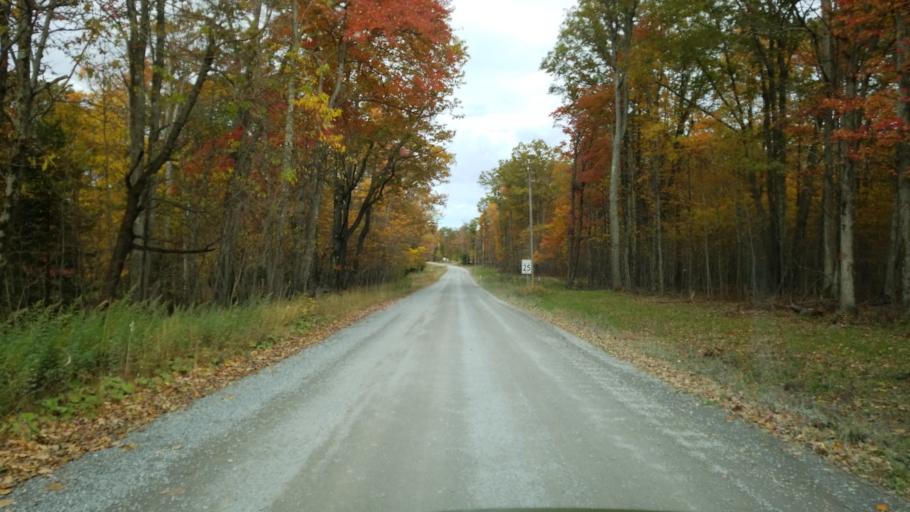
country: US
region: Pennsylvania
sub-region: Clearfield County
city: Clearfield
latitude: 41.1701
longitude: -78.4445
